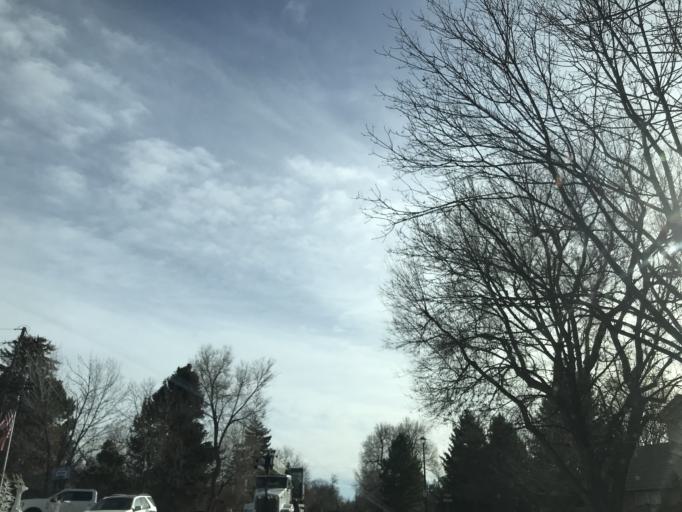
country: US
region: Colorado
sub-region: Arapahoe County
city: Littleton
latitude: 39.5972
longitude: -105.0093
